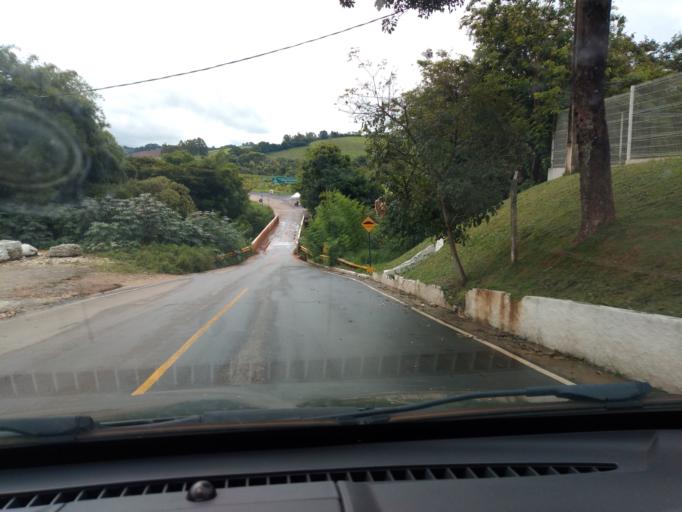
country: BR
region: Minas Gerais
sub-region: Lavras
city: Lavras
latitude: -21.5064
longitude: -44.9152
